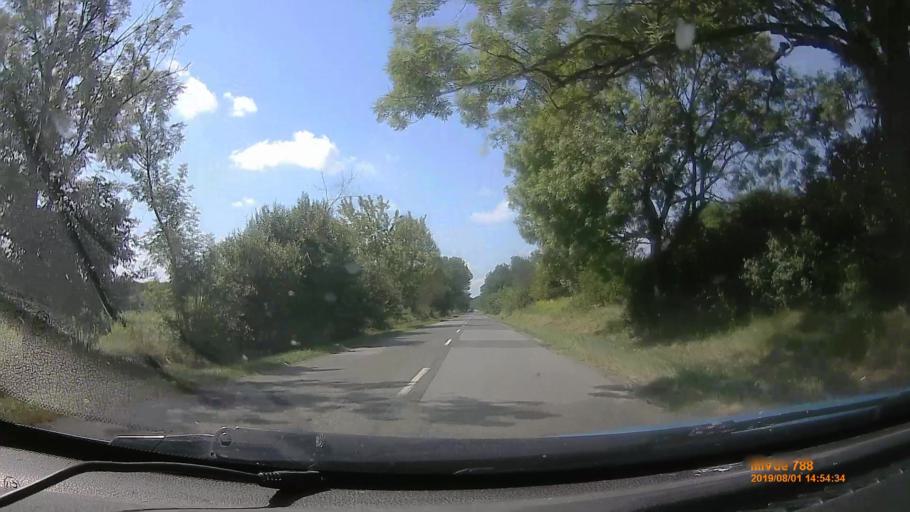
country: HU
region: Baranya
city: Vajszlo
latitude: 45.8656
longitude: 17.9684
